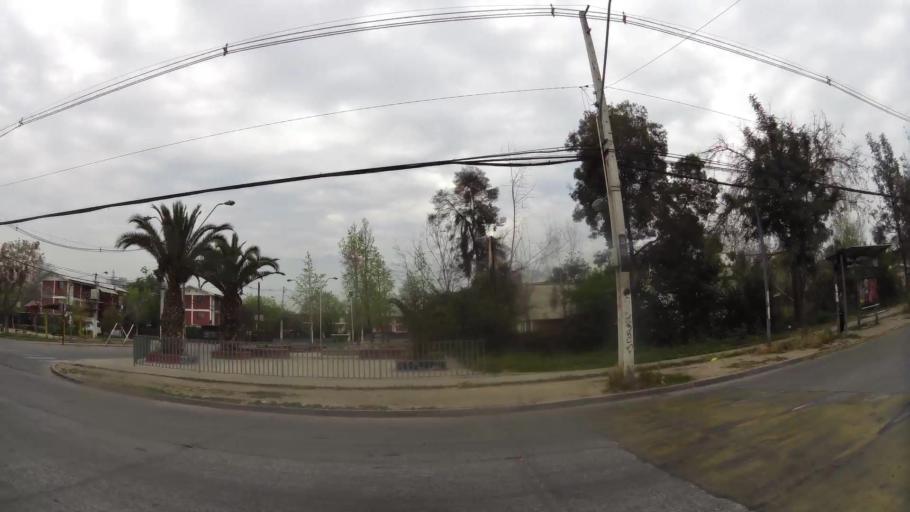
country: CL
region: Santiago Metropolitan
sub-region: Provincia de Santiago
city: Villa Presidente Frei, Nunoa, Santiago, Chile
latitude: -33.5003
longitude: -70.5929
